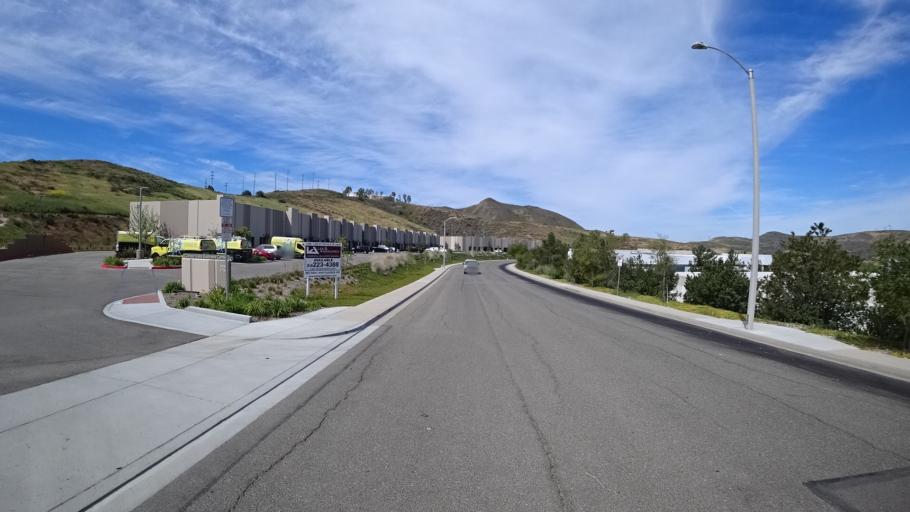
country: US
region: California
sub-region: Ventura County
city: Casa Conejo
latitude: 34.1992
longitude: -118.9317
